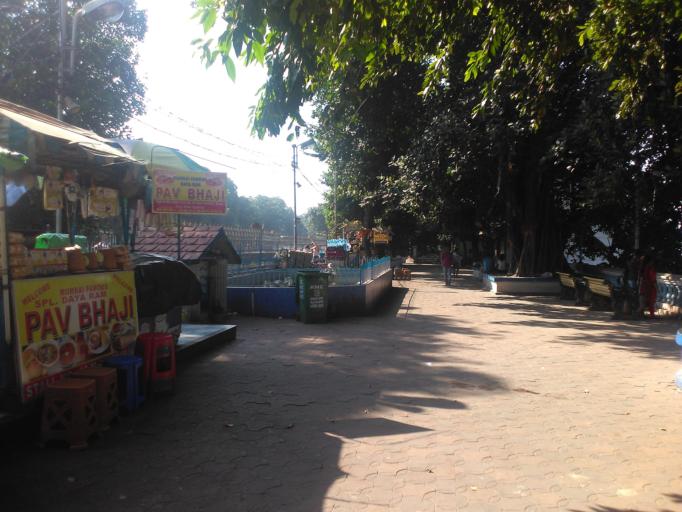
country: IN
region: West Bengal
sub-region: Kolkata
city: Bara Bazar
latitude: 22.5593
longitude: 88.3330
